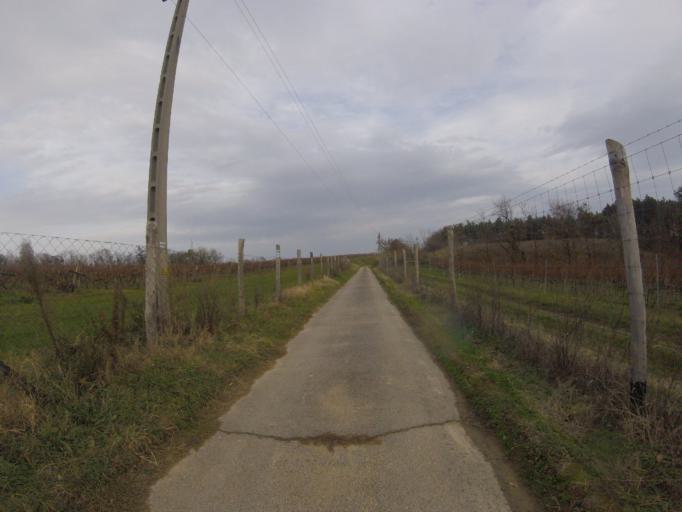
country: HU
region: Tolna
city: Szentgalpuszta
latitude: 46.3475
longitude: 18.6486
